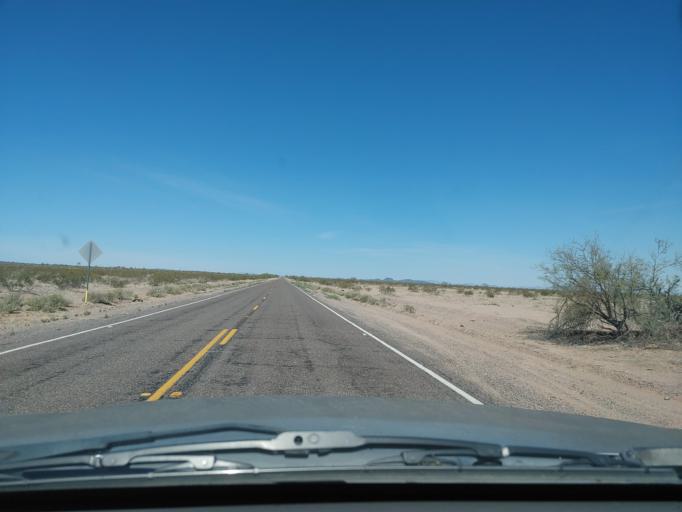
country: US
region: Arizona
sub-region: Maricopa County
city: Gila Bend
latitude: 32.8740
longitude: -113.2163
